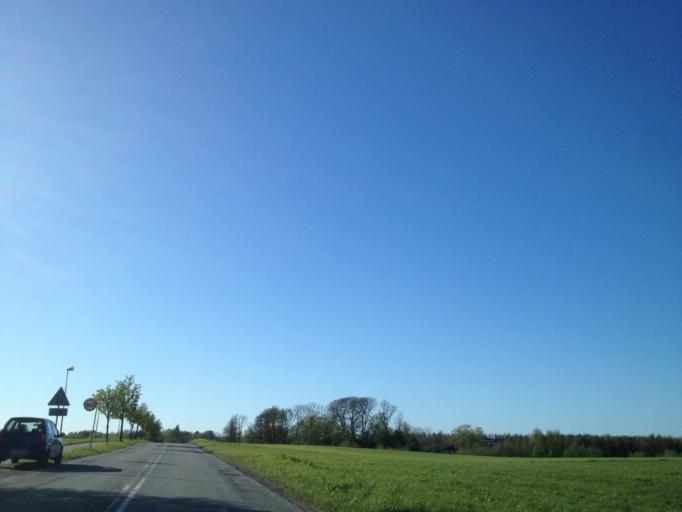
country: DK
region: Zealand
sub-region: Holbaek Kommune
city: Tollose
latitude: 55.5737
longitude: 11.7829
